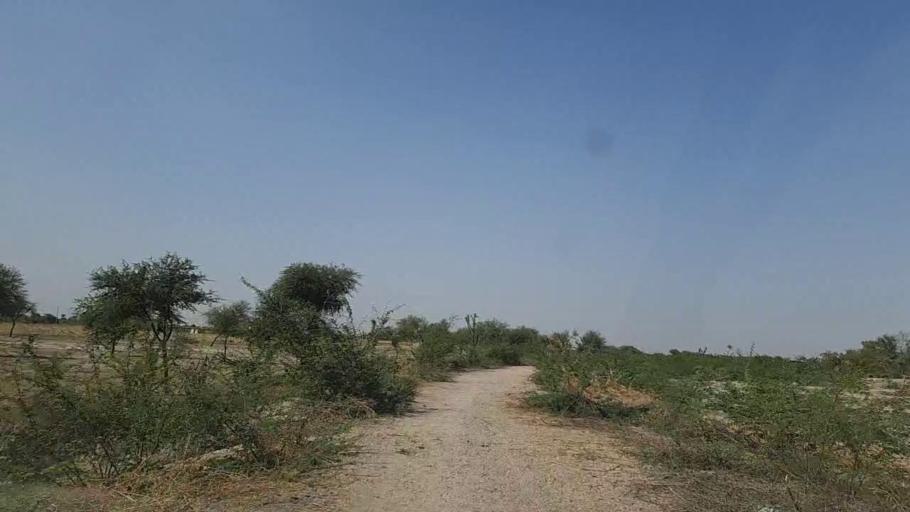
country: PK
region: Sindh
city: Naukot
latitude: 24.6329
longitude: 69.2929
